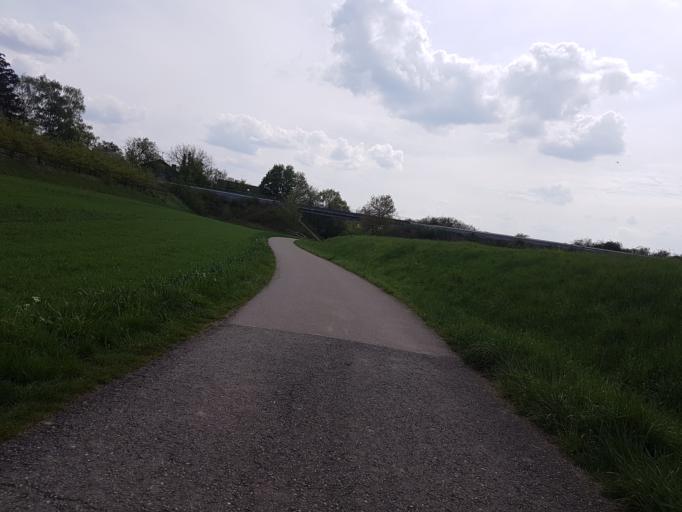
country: DE
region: Baden-Wuerttemberg
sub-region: Regierungsbezirk Stuttgart
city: Herrenberg
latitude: 48.5780
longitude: 8.8729
